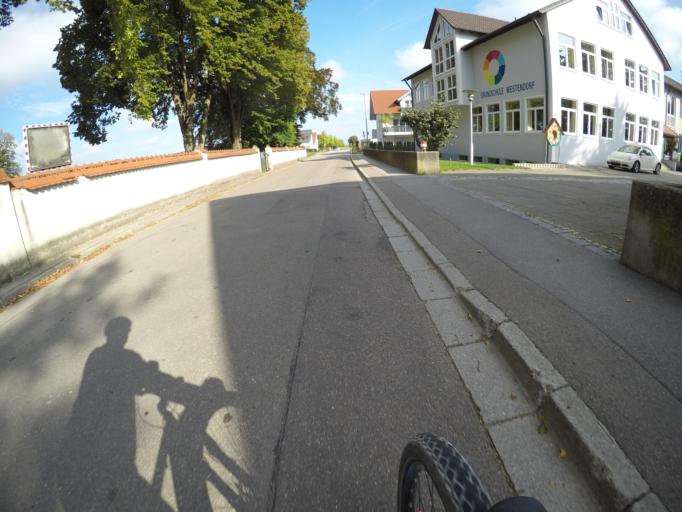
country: DE
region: Bavaria
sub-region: Swabia
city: Westendorf
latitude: 48.5758
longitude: 10.8375
